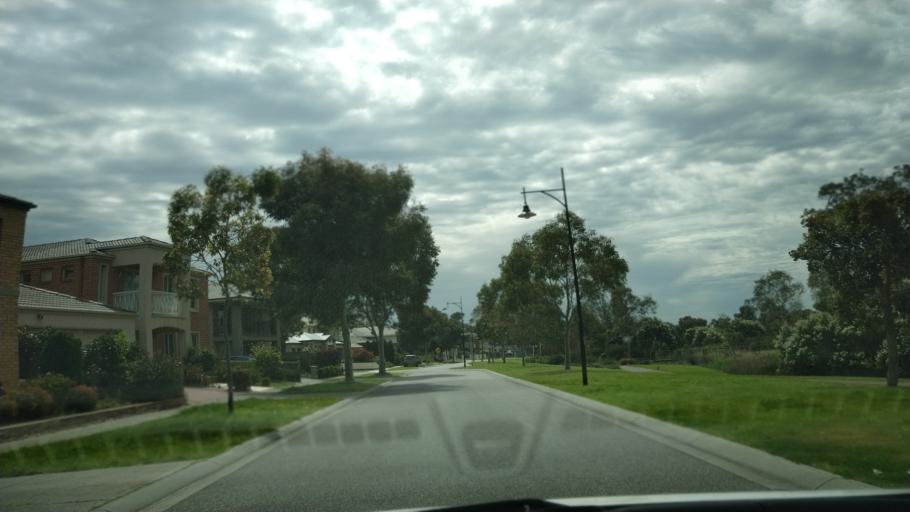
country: AU
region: Victoria
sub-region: Greater Dandenong
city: Keysborough
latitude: -38.0024
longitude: 145.1588
